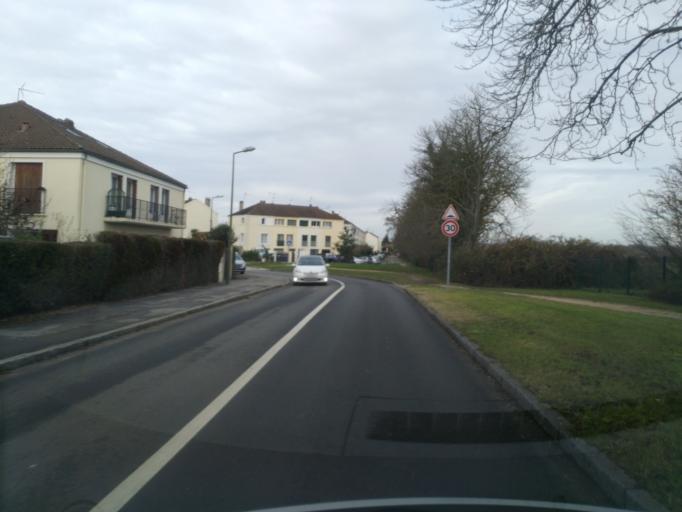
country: FR
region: Ile-de-France
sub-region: Departement des Yvelines
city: Villepreux
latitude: 48.8217
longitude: 2.0005
